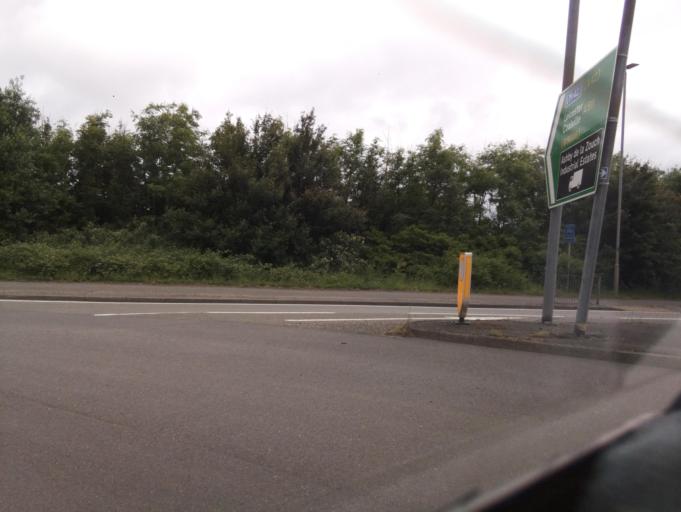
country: GB
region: England
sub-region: Leicestershire
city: Ashby de la Zouch
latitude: 52.7673
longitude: -1.5024
